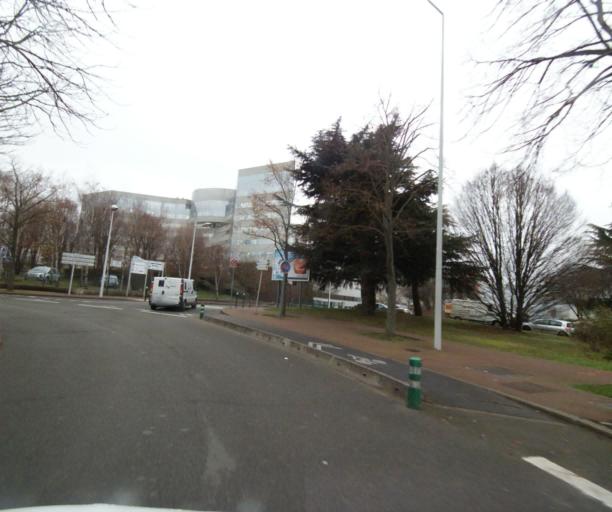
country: FR
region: Ile-de-France
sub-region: Departement des Hauts-de-Seine
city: Nanterre
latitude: 48.8919
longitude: 2.2143
